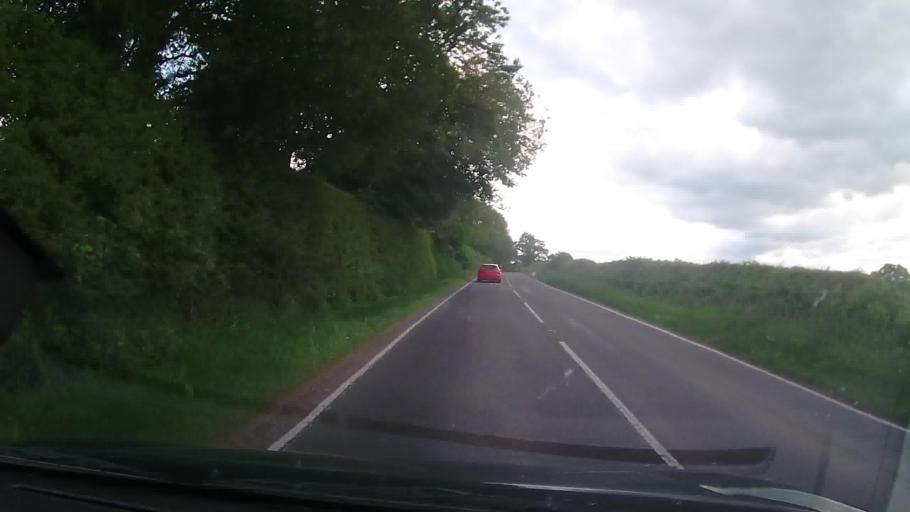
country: GB
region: England
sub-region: Shropshire
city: Wem
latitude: 52.8291
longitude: -2.7343
